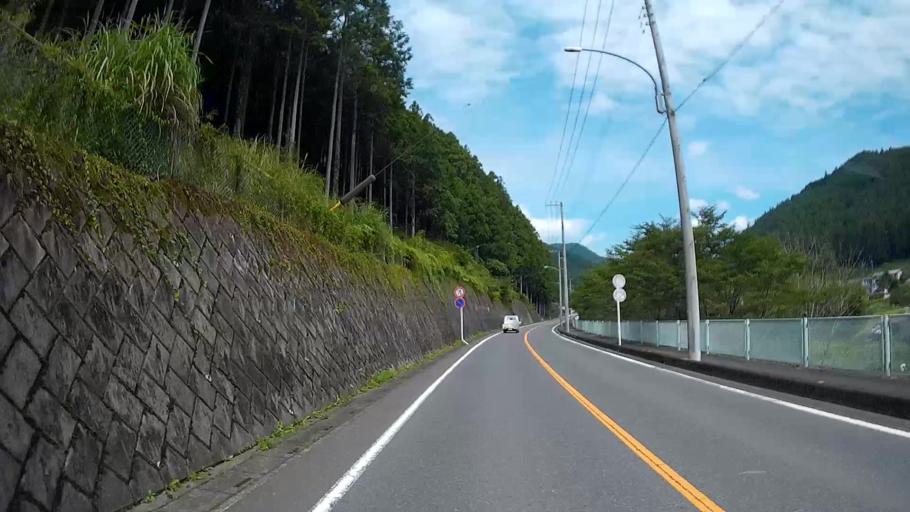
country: JP
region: Tokyo
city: Ome
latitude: 35.8580
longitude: 139.1900
